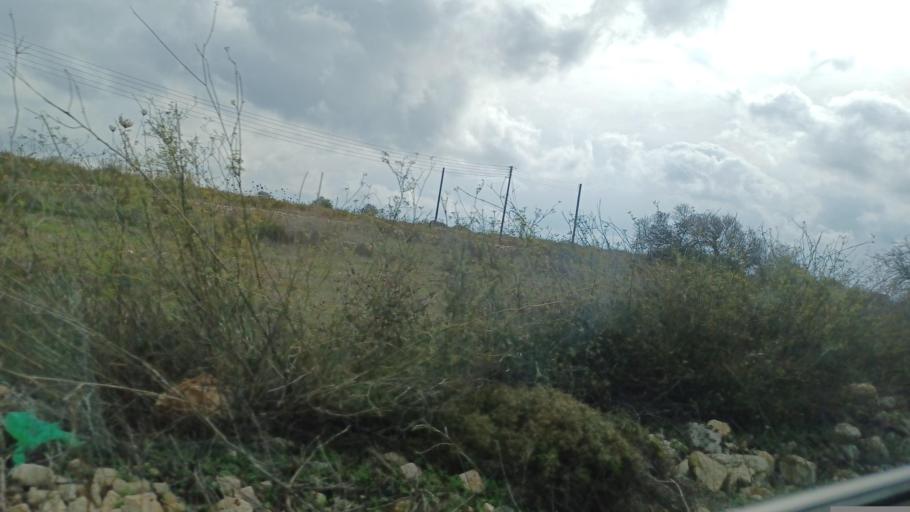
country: CY
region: Pafos
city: Pegeia
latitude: 34.9534
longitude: 32.4030
